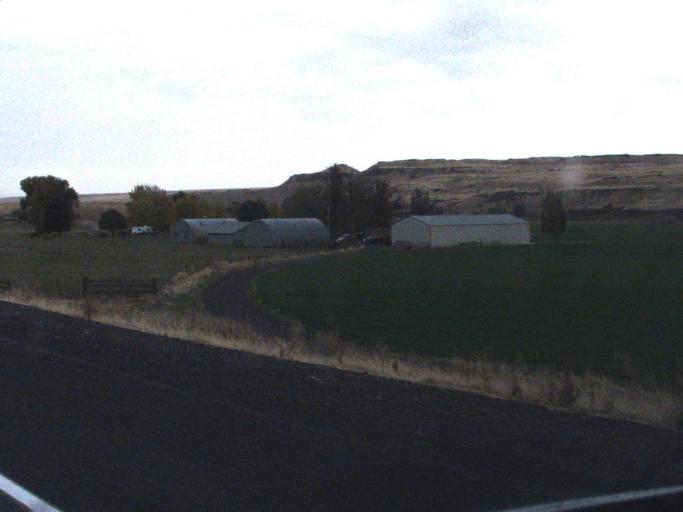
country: US
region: Washington
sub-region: Columbia County
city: Dayton
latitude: 46.7771
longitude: -118.0665
